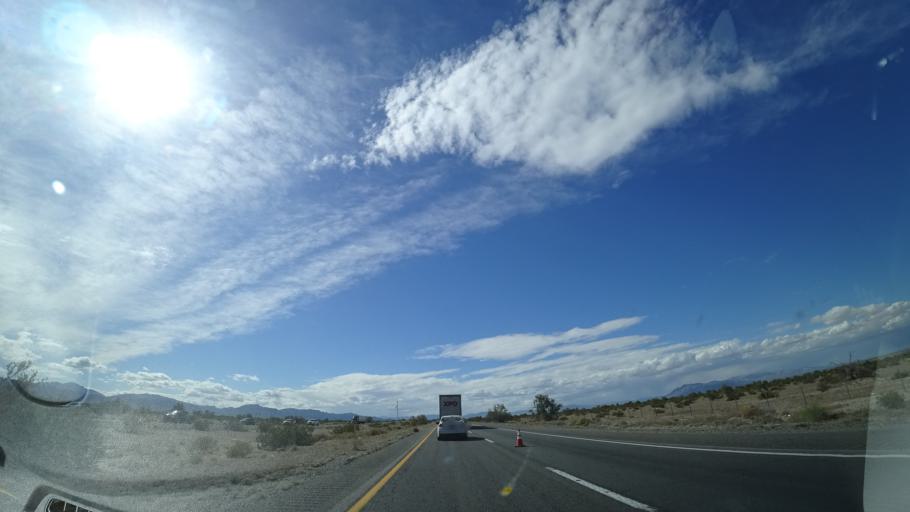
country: US
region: California
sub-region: Riverside County
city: Mesa Verde
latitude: 33.6556
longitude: -115.1518
